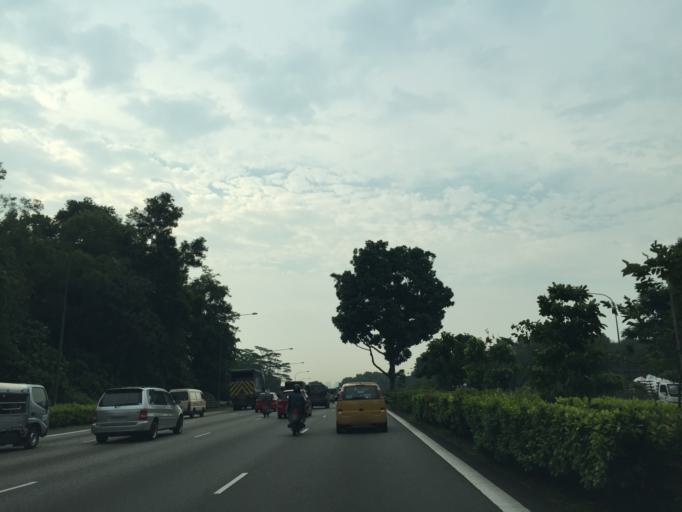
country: MY
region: Johor
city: Johor Bahru
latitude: 1.4003
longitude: 103.7737
